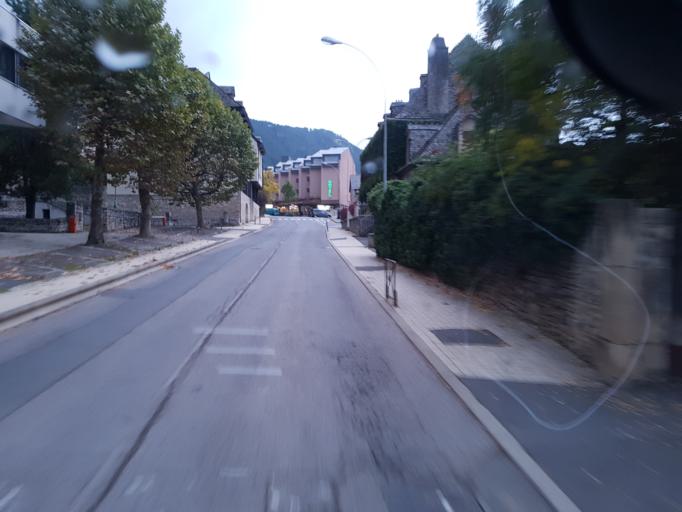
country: FR
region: Languedoc-Roussillon
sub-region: Departement de la Lozere
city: Mende
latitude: 44.5205
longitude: 3.4980
